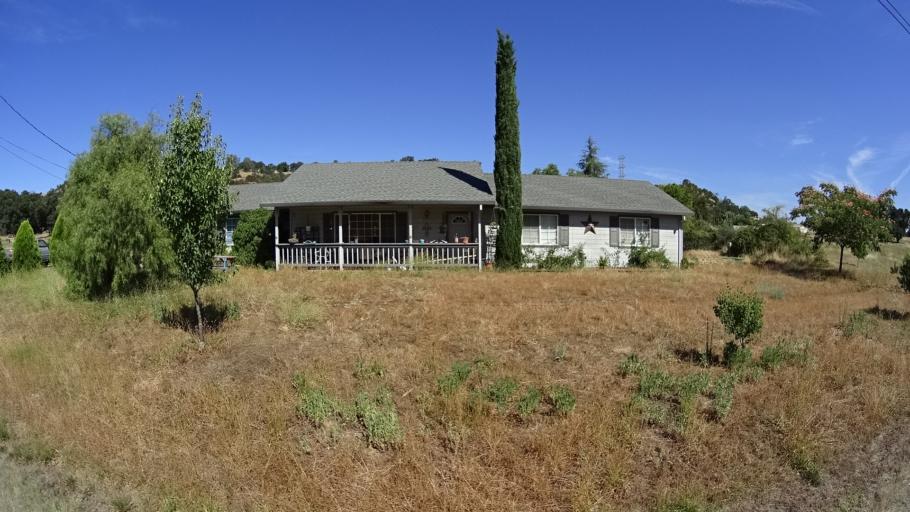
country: US
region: California
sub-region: Calaveras County
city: Rancho Calaveras
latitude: 38.1558
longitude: -120.8536
